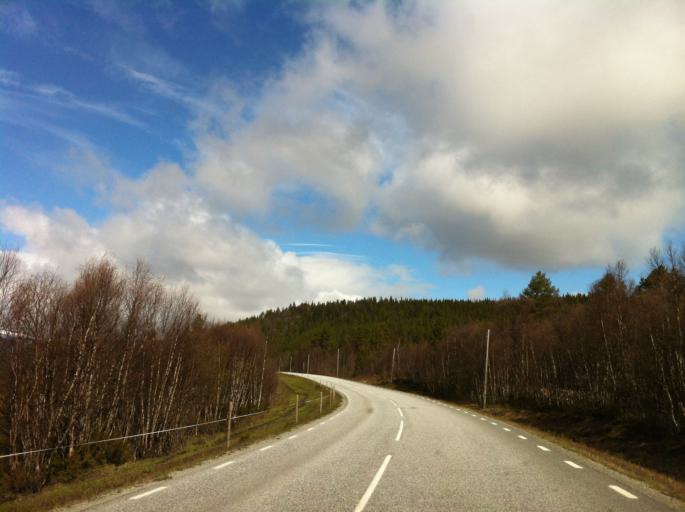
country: SE
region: Jaemtland
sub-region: Are Kommun
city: Are
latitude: 62.5999
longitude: 12.5258
